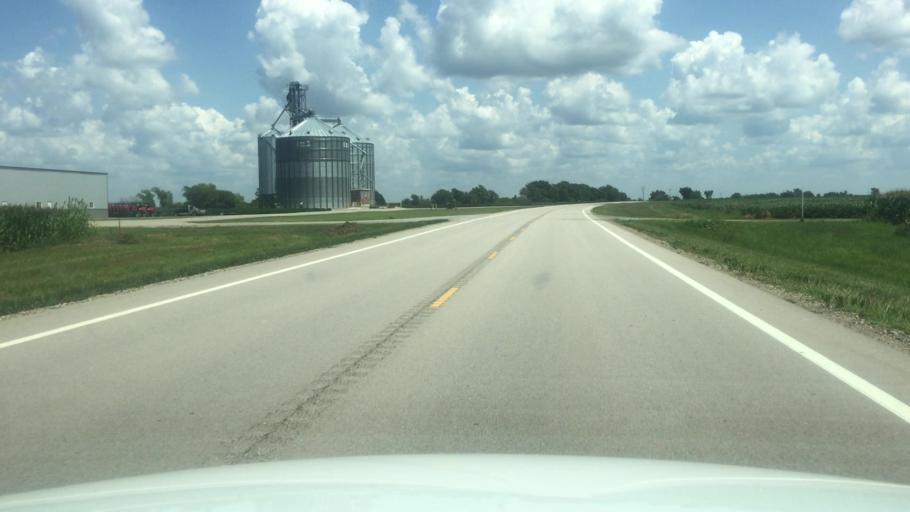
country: US
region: Kansas
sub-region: Brown County
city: Horton
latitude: 39.6603
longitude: -95.3875
